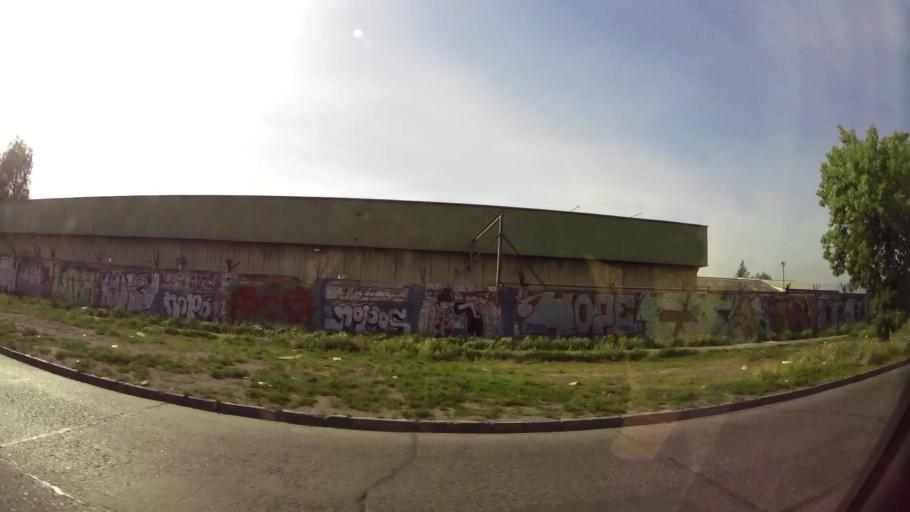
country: CL
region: Santiago Metropolitan
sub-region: Provincia de Santiago
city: La Pintana
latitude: -33.5275
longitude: -70.6253
